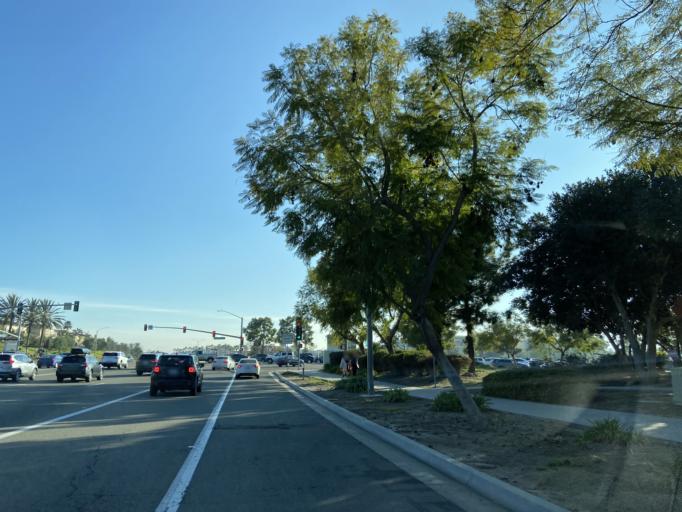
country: US
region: California
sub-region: San Diego County
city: Bonita
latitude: 32.6285
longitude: -116.9647
